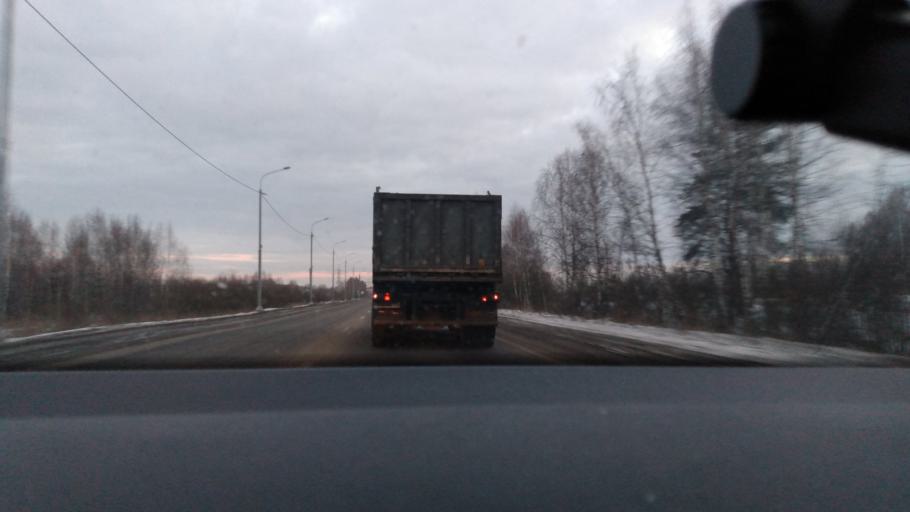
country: RU
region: Moskovskaya
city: Yegor'yevsk
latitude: 55.4112
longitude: 39.0498
